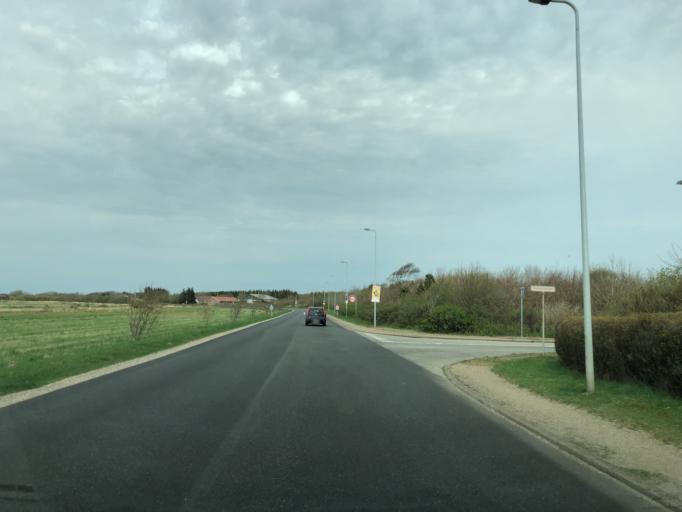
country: DK
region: Central Jutland
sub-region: Ringkobing-Skjern Kommune
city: Skjern
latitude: 55.9477
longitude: 8.4819
